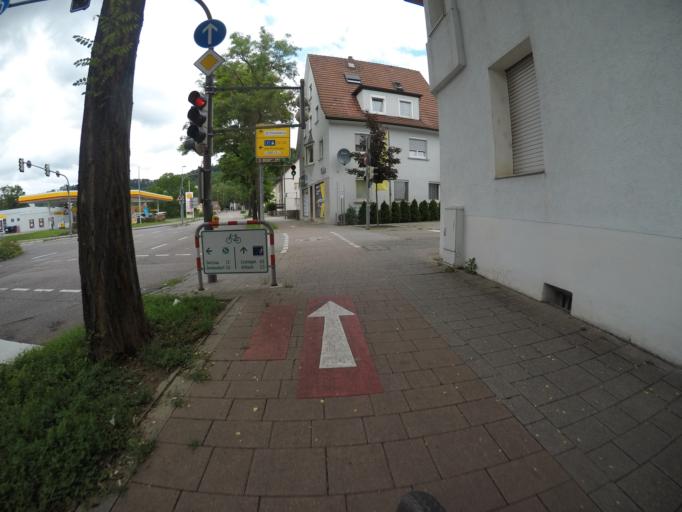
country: DE
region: Baden-Wuerttemberg
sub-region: Regierungsbezirk Stuttgart
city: Plochingen
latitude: 48.7153
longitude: 9.4144
